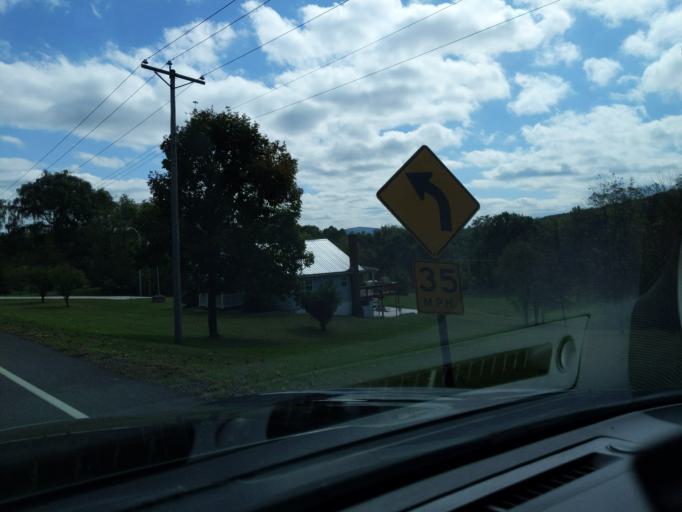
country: US
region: Pennsylvania
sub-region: Blair County
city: Altoona
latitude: 40.4904
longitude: -78.4426
